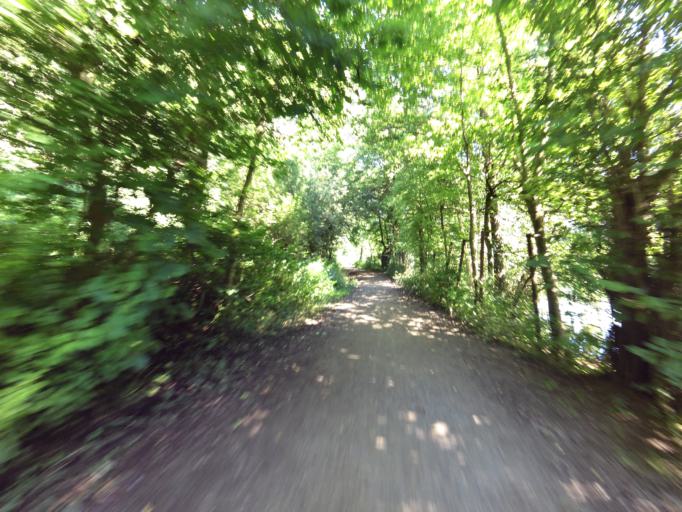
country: DE
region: North Rhine-Westphalia
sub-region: Regierungsbezirk Koln
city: Wurselen
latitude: 50.8294
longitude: 6.1021
